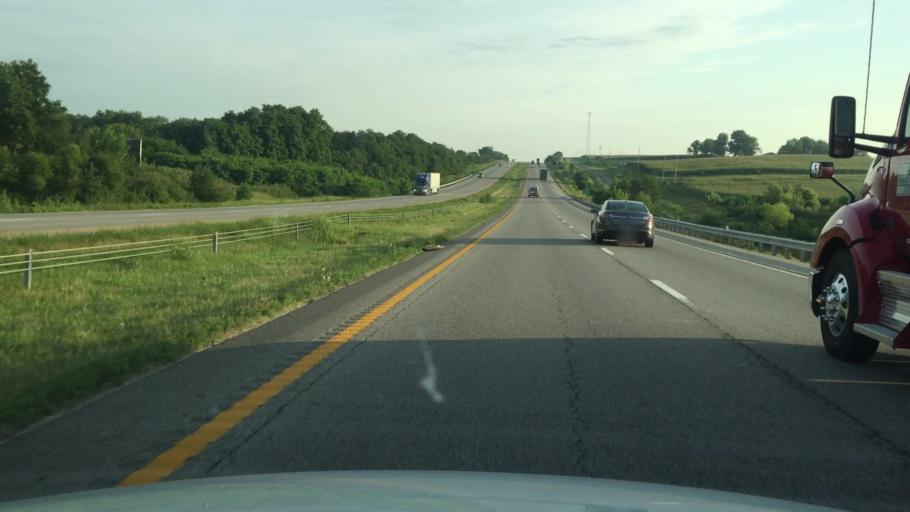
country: US
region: Missouri
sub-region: Platte County
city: Platte City
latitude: 39.5389
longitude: -94.7874
